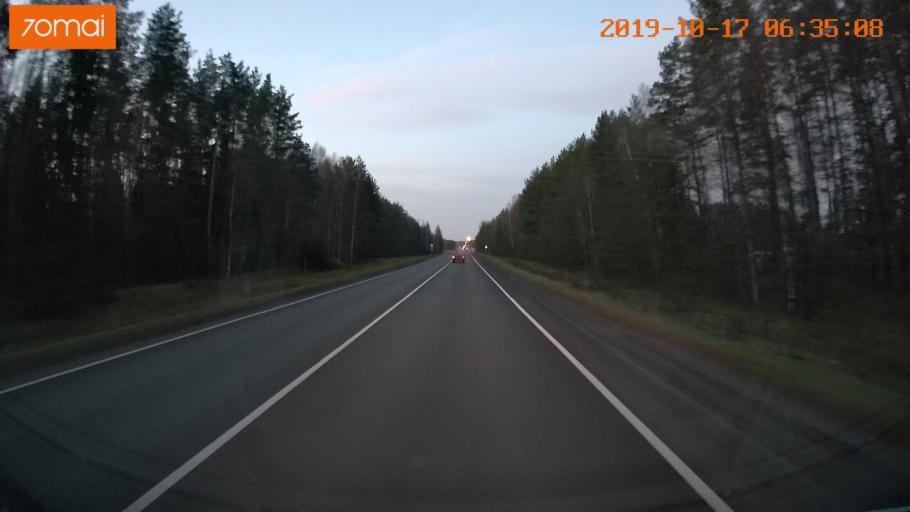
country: RU
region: Ivanovo
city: Novoye Leushino
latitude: 56.6955
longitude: 40.6264
